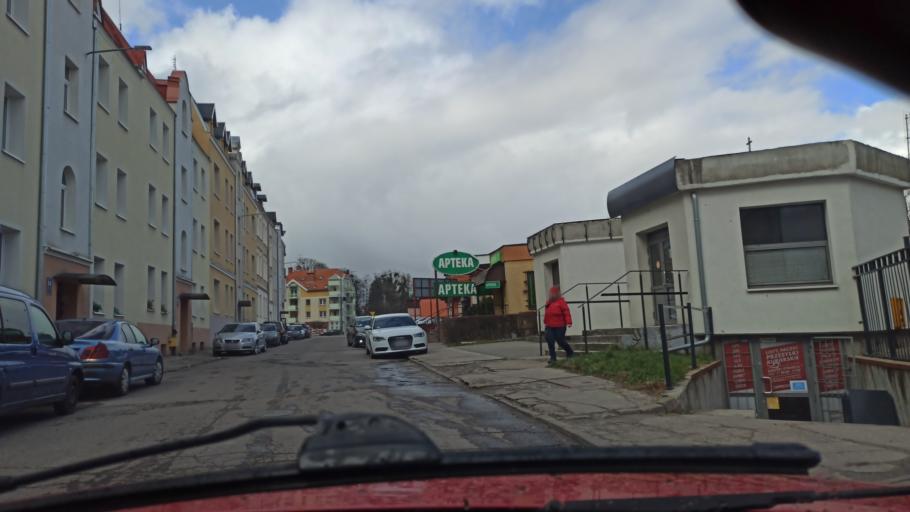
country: PL
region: Warmian-Masurian Voivodeship
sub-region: Powiat elblaski
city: Elblag
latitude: 54.1578
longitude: 19.4134
